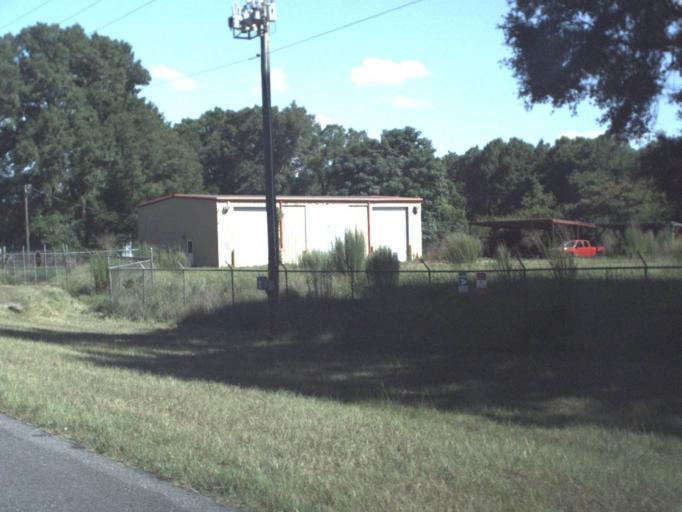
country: US
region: Florida
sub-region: Alachua County
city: High Springs
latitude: 29.8386
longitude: -82.6233
